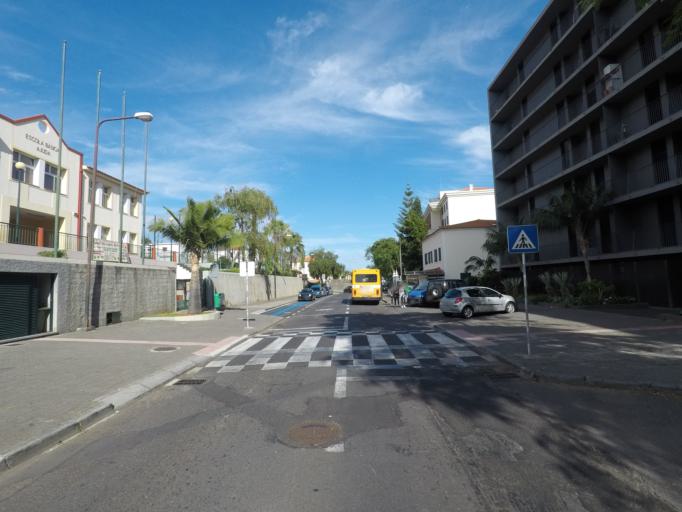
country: PT
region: Madeira
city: Camara de Lobos
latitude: 32.6390
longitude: -16.9423
